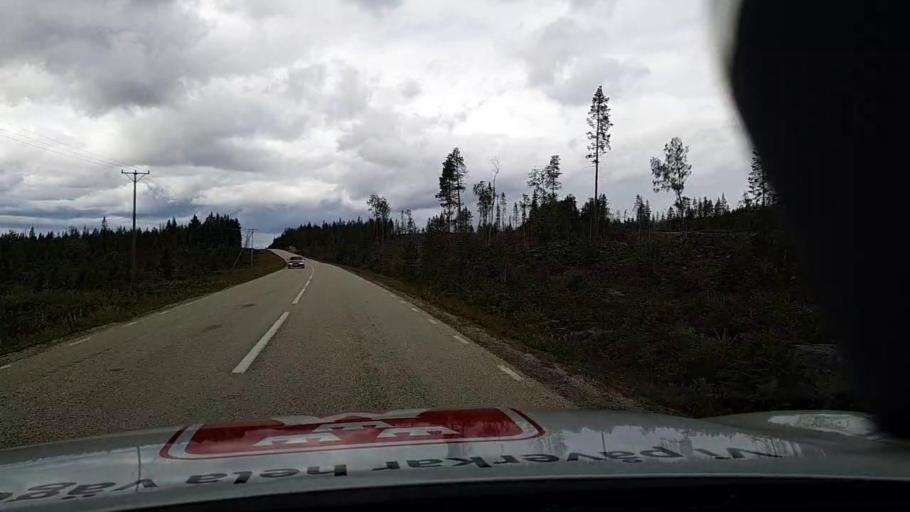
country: SE
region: Jaemtland
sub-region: Are Kommun
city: Jarpen
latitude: 62.7670
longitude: 13.7245
